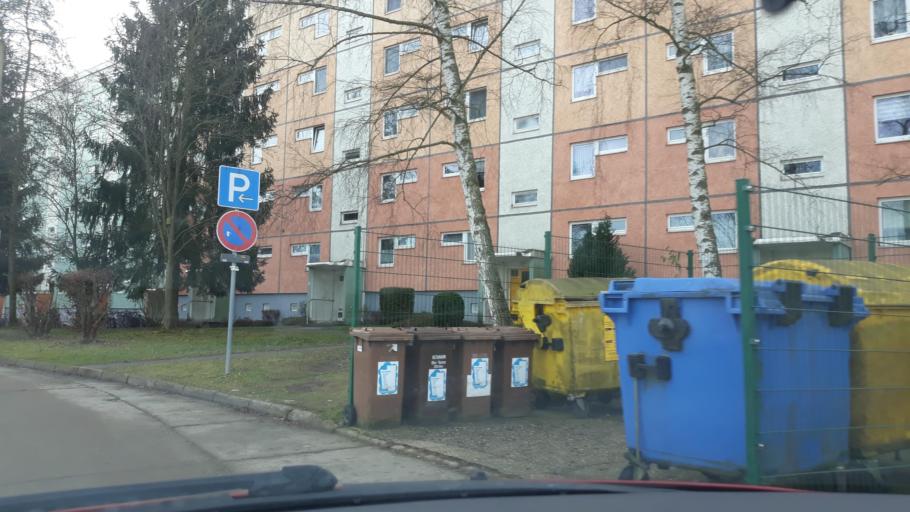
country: DE
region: Saxony
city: Kirchberg
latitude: 50.6172
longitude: 12.5143
